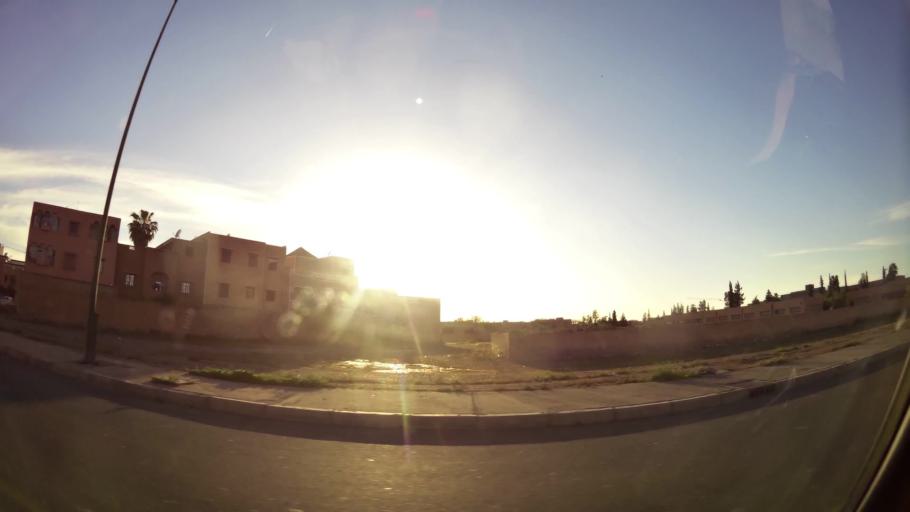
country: MA
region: Marrakech-Tensift-Al Haouz
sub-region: Marrakech
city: Marrakesh
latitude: 31.6204
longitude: -8.0442
